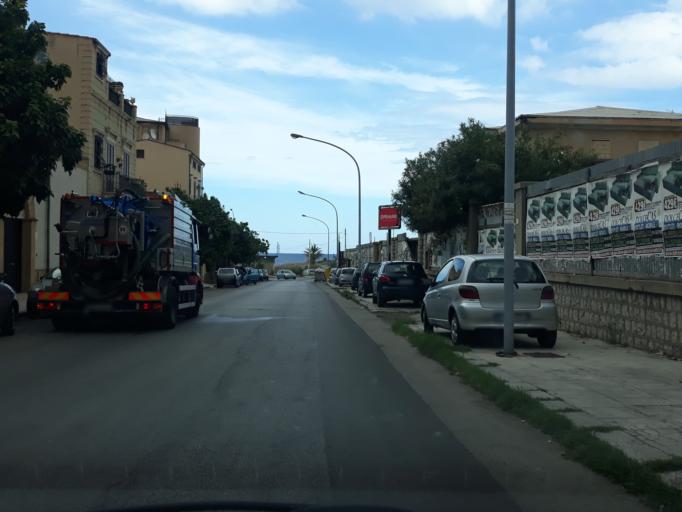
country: IT
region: Sicily
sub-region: Palermo
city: Ciaculli
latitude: 38.1018
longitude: 13.3942
